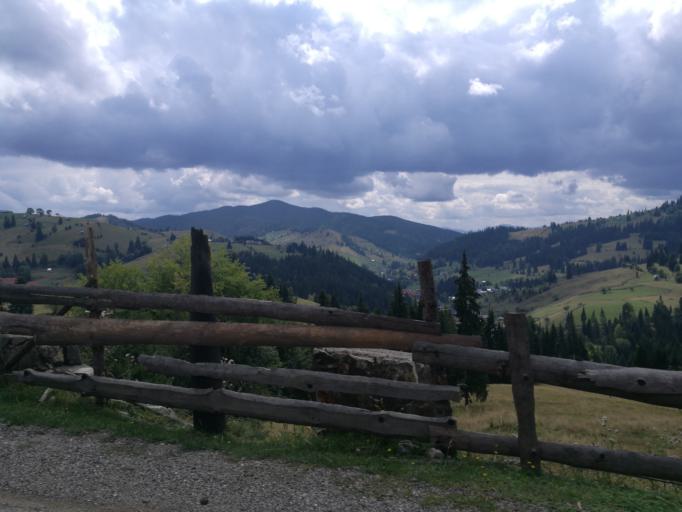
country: RO
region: Suceava
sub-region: Comuna Vatra Moldovitei
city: Vatra Moldovitei
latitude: 47.7264
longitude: 25.6128
